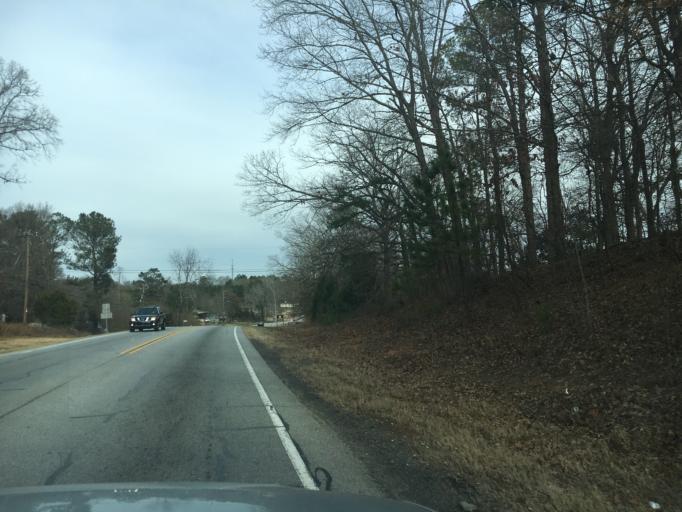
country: US
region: Georgia
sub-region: Barrow County
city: Winder
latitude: 33.9835
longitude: -83.7350
